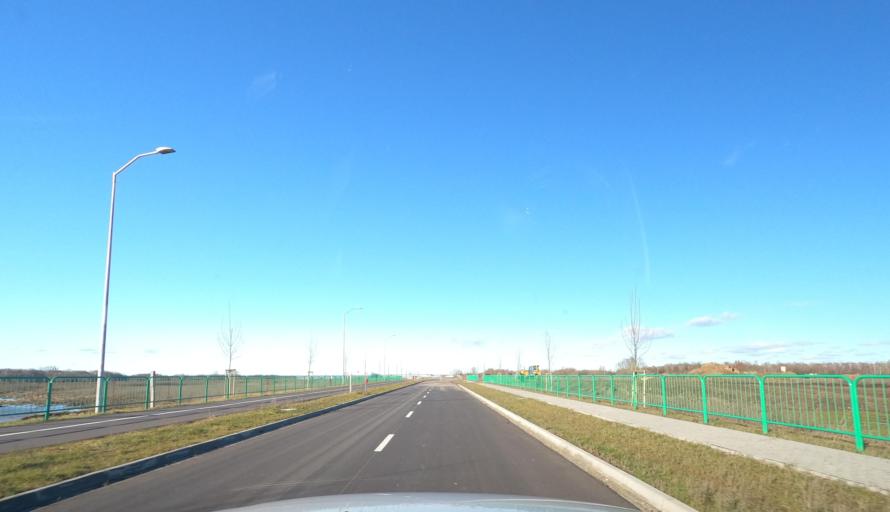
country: PL
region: West Pomeranian Voivodeship
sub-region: Powiat pyrzycki
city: Warnice
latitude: 53.2713
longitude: 14.9834
